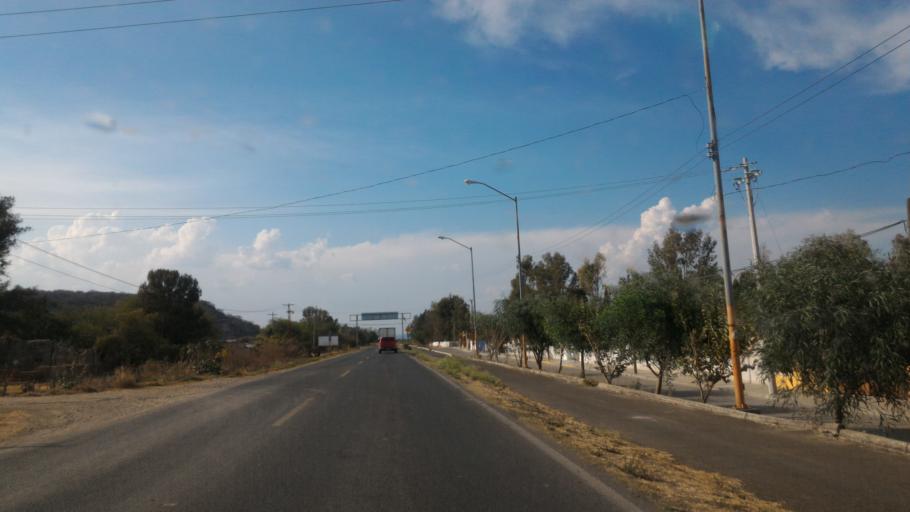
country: MX
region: Guanajuato
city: Ciudad Manuel Doblado
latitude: 20.7428
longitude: -101.9571
